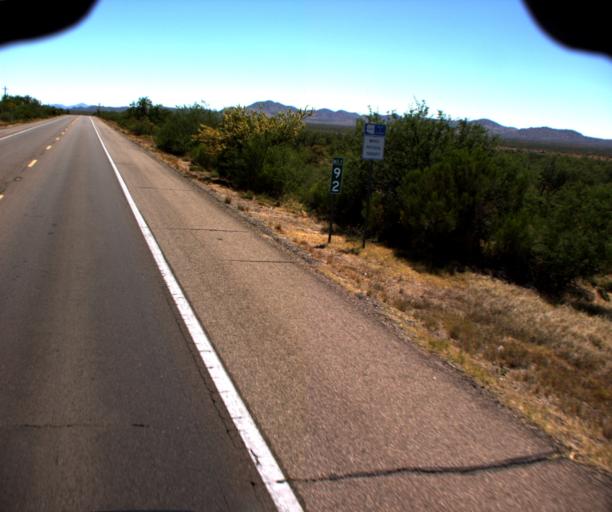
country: US
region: Arizona
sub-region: Pima County
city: Catalina
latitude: 32.5675
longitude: -110.9256
